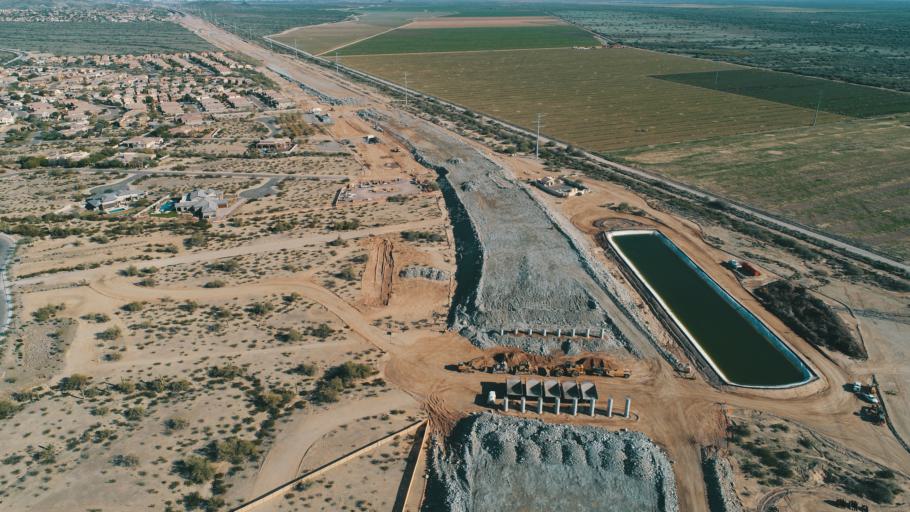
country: US
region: Arizona
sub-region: Maricopa County
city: Laveen
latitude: 33.2935
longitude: -112.1344
